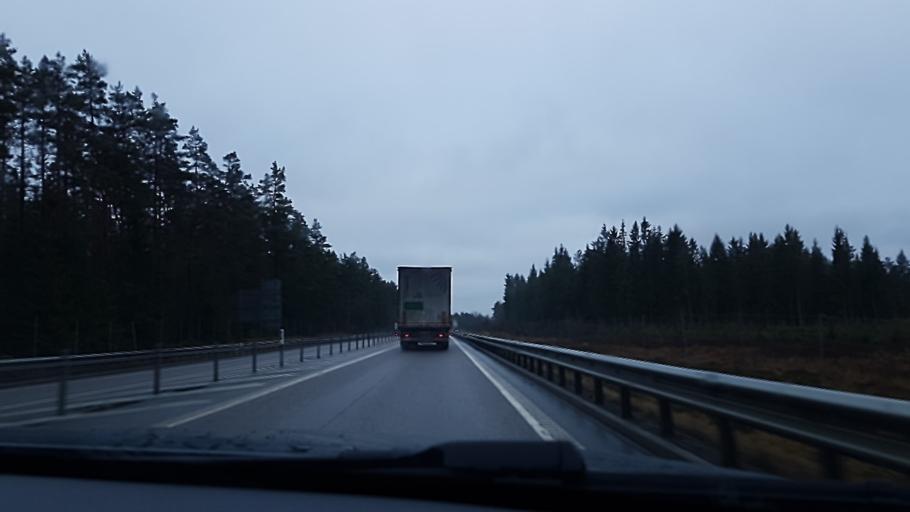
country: SE
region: Kronoberg
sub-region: Ljungby Kommun
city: Lagan
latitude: 56.9498
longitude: 14.0005
